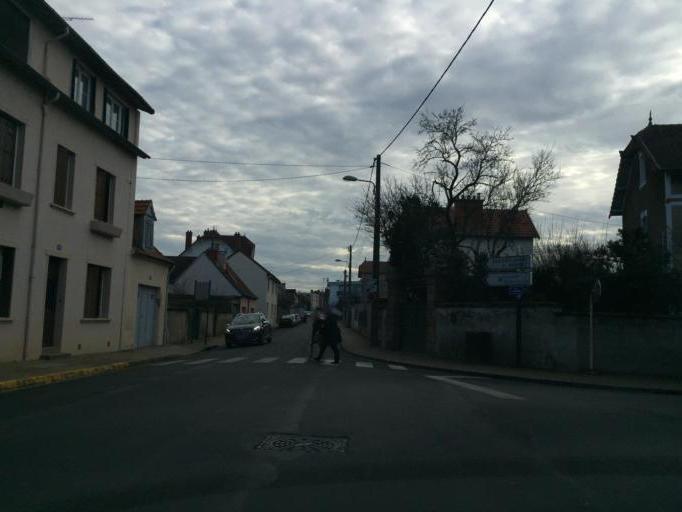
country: FR
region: Auvergne
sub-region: Departement de l'Allier
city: Moulins
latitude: 46.5733
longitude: 3.3357
